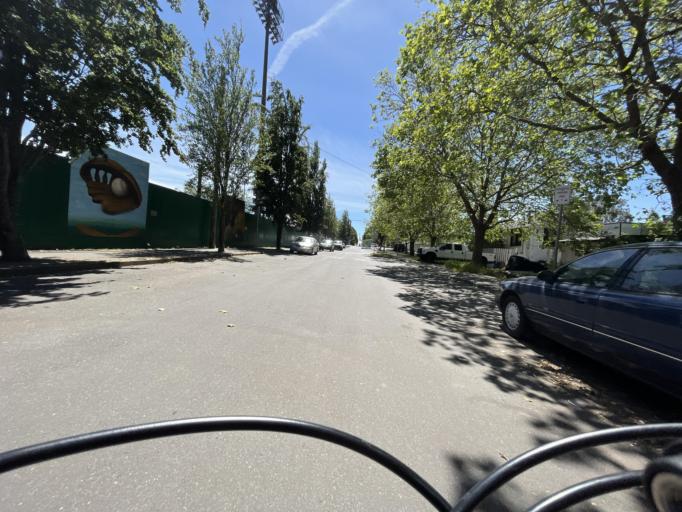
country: CA
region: British Columbia
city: Victoria
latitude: 48.4318
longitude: -123.3556
